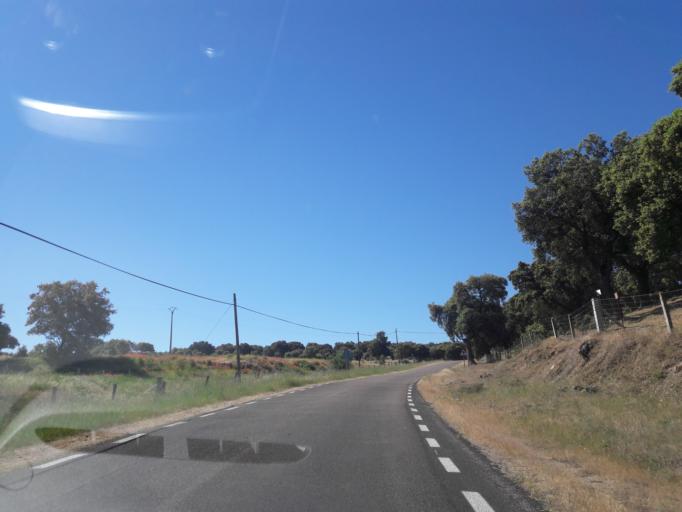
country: ES
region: Castille and Leon
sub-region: Provincia de Salamanca
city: Juzbado
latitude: 41.0673
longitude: -5.8991
